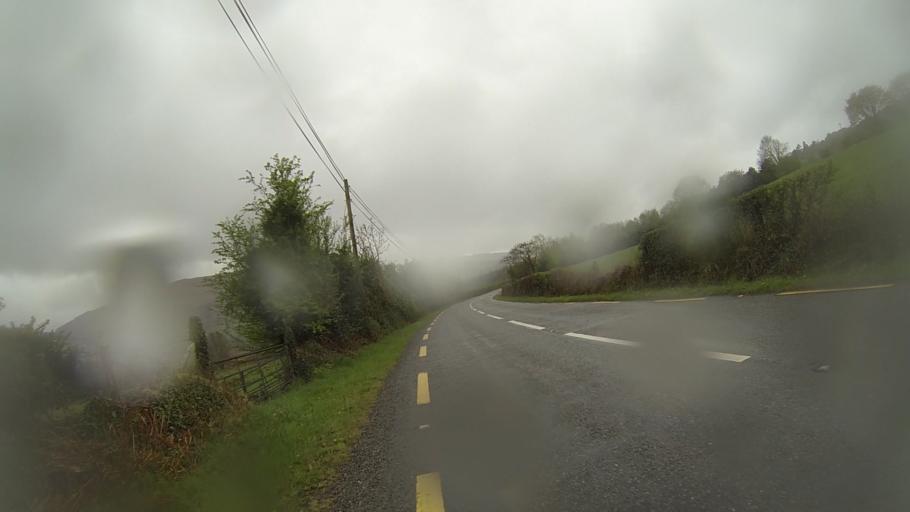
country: IE
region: Munster
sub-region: Ciarrai
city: Kenmare
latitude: 51.8235
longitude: -9.5268
